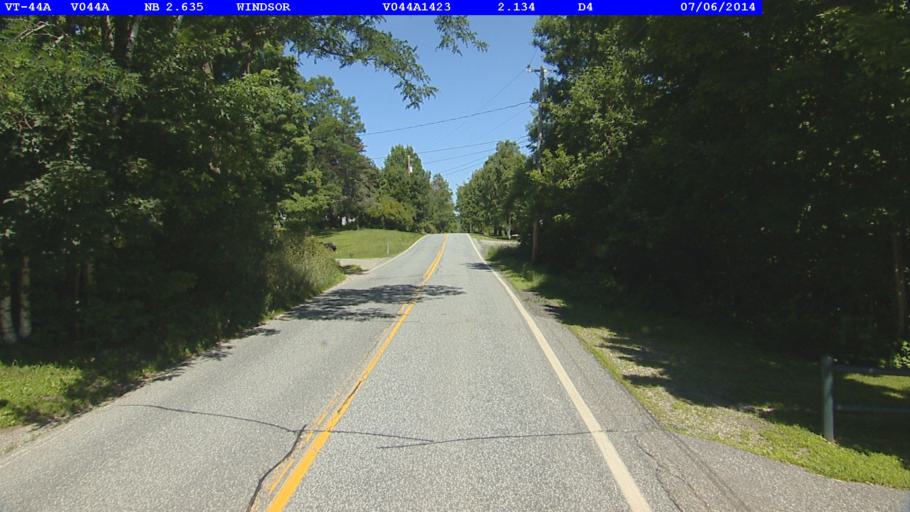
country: US
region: Vermont
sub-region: Windsor County
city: Windsor
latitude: 43.4554
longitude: -72.4197
